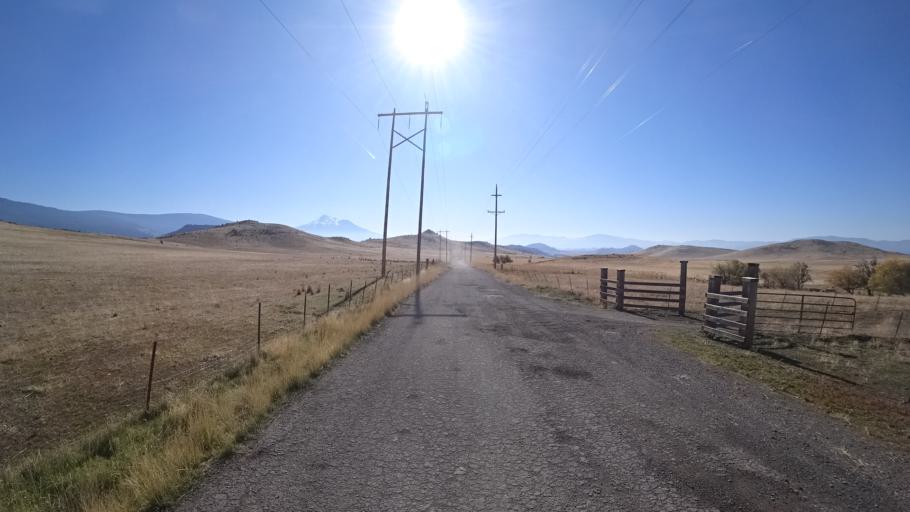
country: US
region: California
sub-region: Siskiyou County
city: Montague
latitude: 41.7578
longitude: -122.3593
